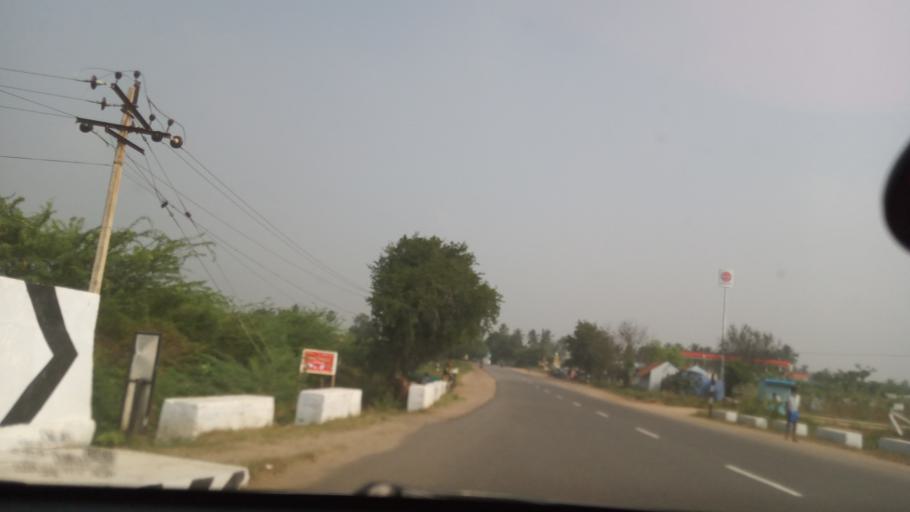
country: IN
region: Tamil Nadu
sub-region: Erode
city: Punjai Puliyampatti
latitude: 11.4050
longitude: 77.1926
